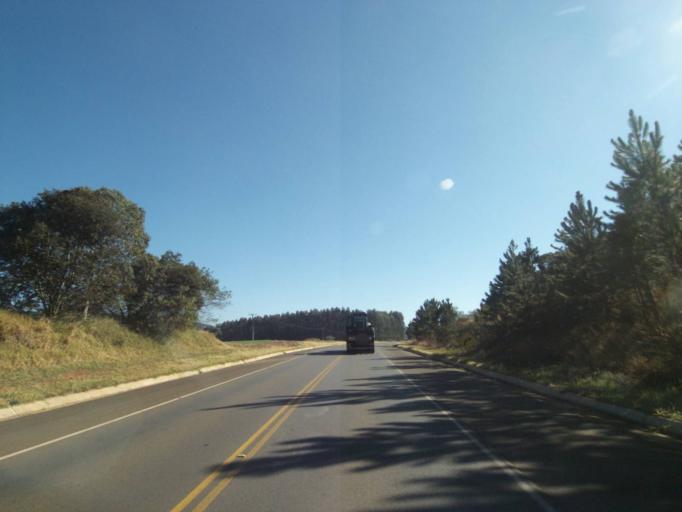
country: BR
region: Parana
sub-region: Tibagi
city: Tibagi
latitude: -24.4779
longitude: -50.4449
